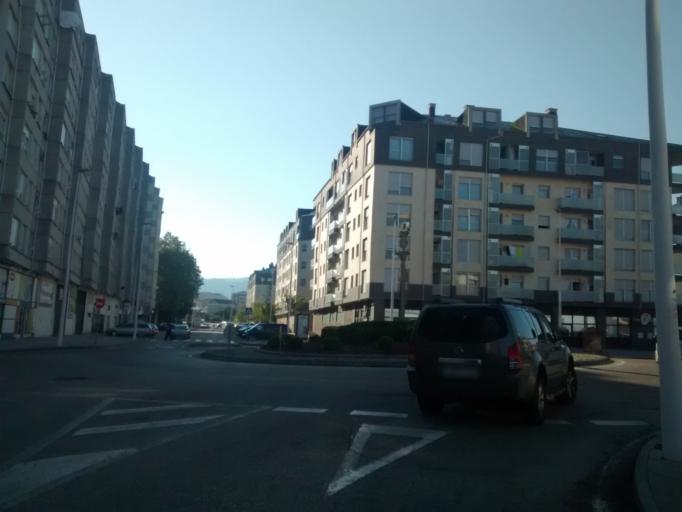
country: ES
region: Cantabria
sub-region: Provincia de Cantabria
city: Torrelavega
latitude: 43.3475
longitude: -4.0557
